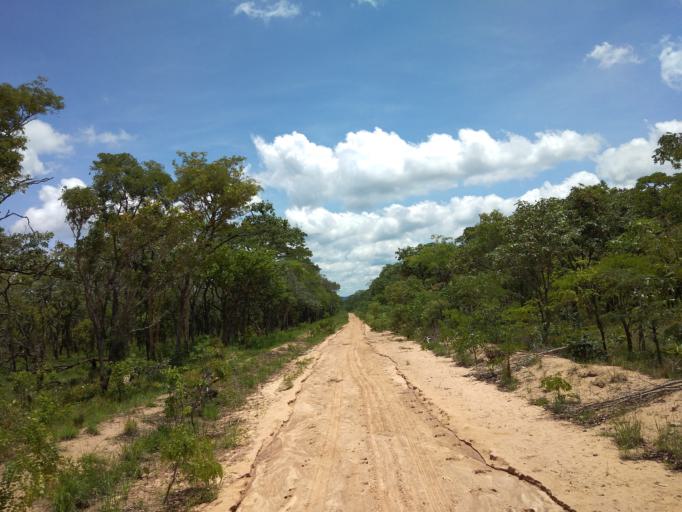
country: ZM
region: Central
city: Mkushi
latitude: -13.9365
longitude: 29.8639
